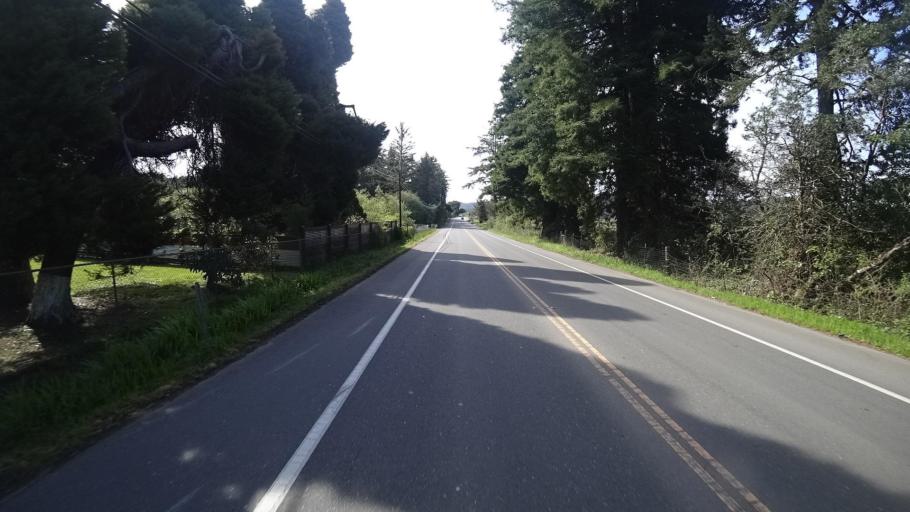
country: US
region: California
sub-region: Humboldt County
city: Myrtletown
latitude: 40.7929
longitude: -124.0863
